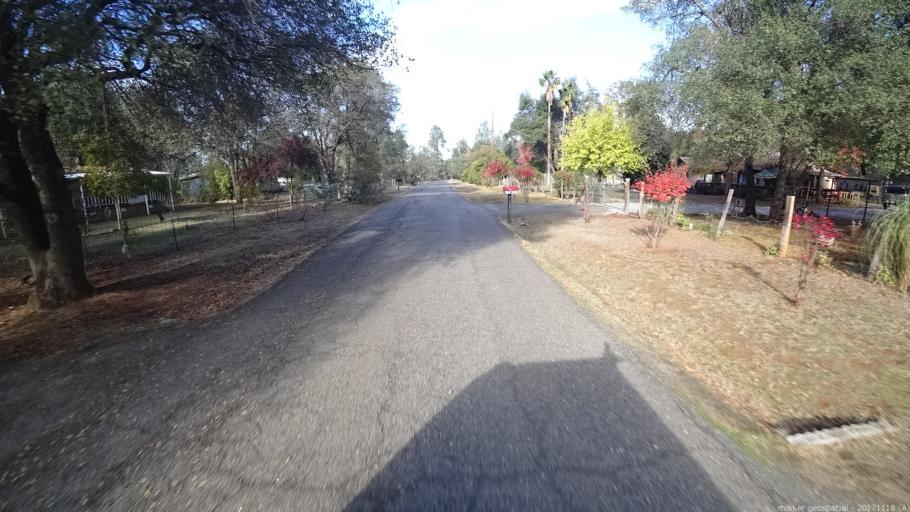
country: US
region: California
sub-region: Shasta County
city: Redding
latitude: 40.4712
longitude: -122.4154
